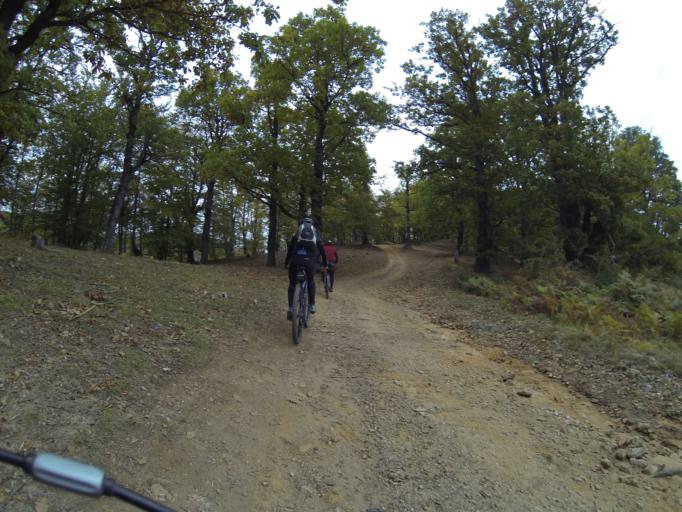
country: RO
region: Gorj
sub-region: Comuna Tismana
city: Sohodol
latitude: 45.0702
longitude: 22.8619
